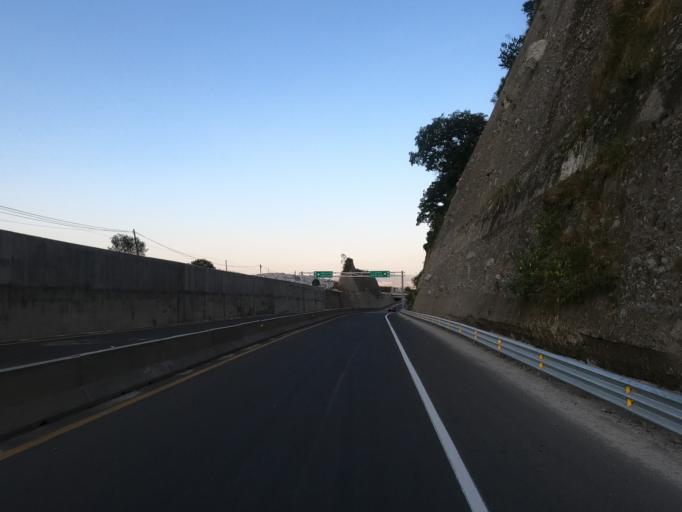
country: MX
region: Mexico
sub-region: Naucalpan de Juarez
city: Ejido el Castillo
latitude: 19.4393
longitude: -99.3014
